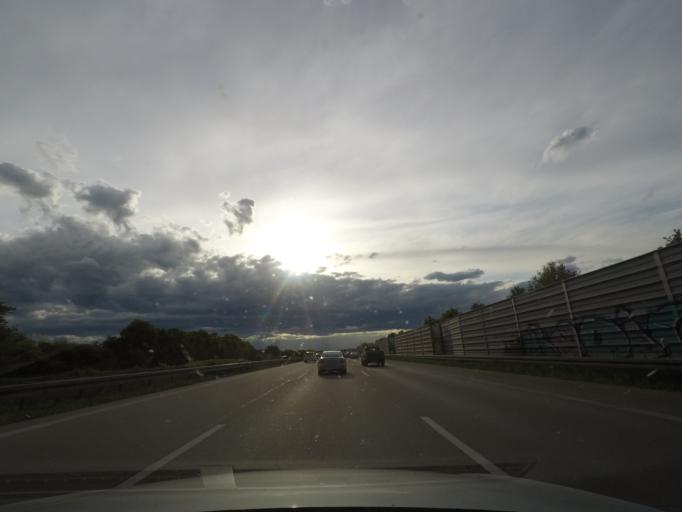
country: DE
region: Saxony-Anhalt
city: Wefensleben
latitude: 52.2054
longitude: 11.1773
